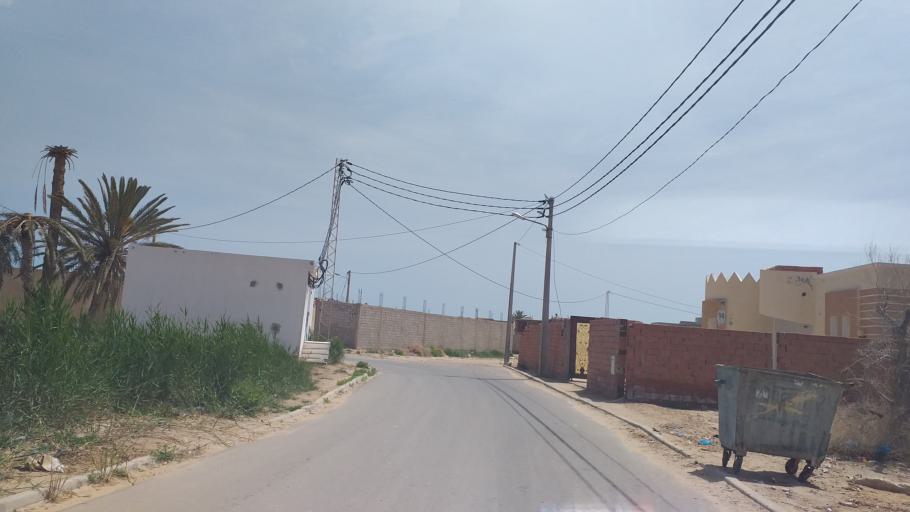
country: TN
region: Qabis
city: Gabes
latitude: 33.9464
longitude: 10.0639
